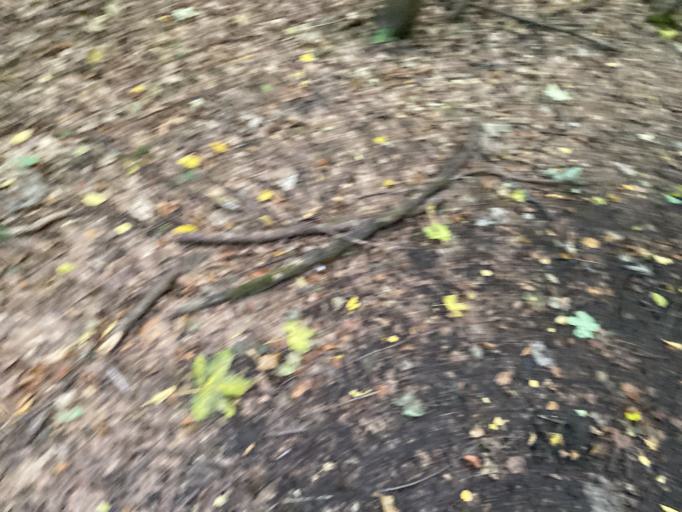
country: DE
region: North Rhine-Westphalia
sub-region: Regierungsbezirk Detmold
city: Kirchlengern
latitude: 52.1775
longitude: 8.6420
